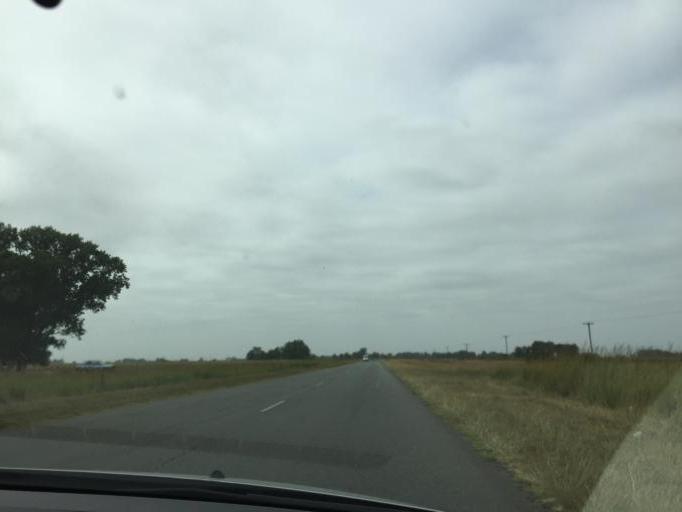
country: AR
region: Buenos Aires
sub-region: Partido de Las Flores
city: Las Flores
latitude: -36.1797
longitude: -59.0609
